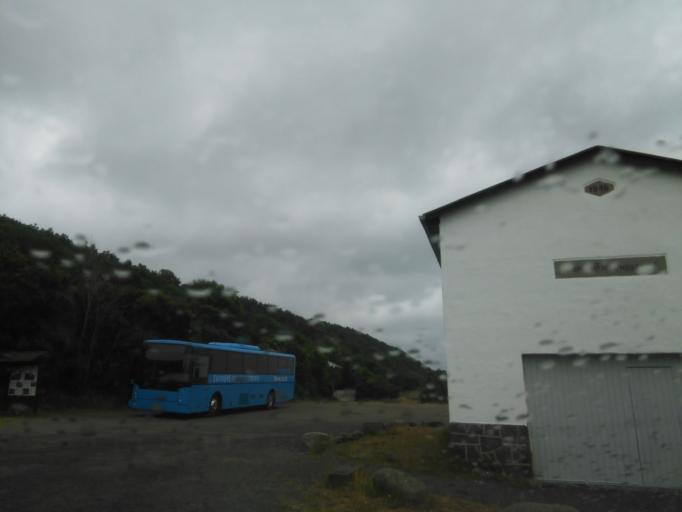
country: DK
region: Capital Region
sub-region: Bornholm Kommune
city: Ronne
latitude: 55.2481
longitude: 14.7355
